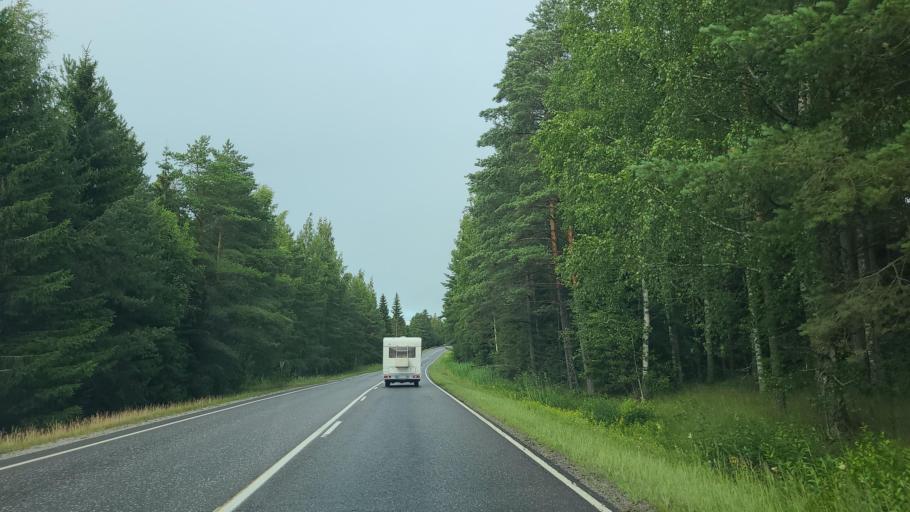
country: FI
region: Varsinais-Suomi
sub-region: Turku
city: Sauvo
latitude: 60.3117
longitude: 22.6895
